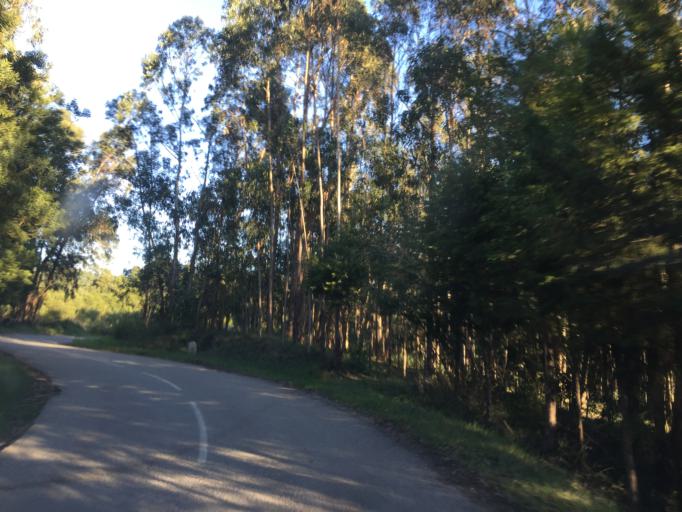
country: PT
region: Coimbra
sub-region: Figueira da Foz
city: Alhadas
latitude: 40.1616
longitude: -8.8018
